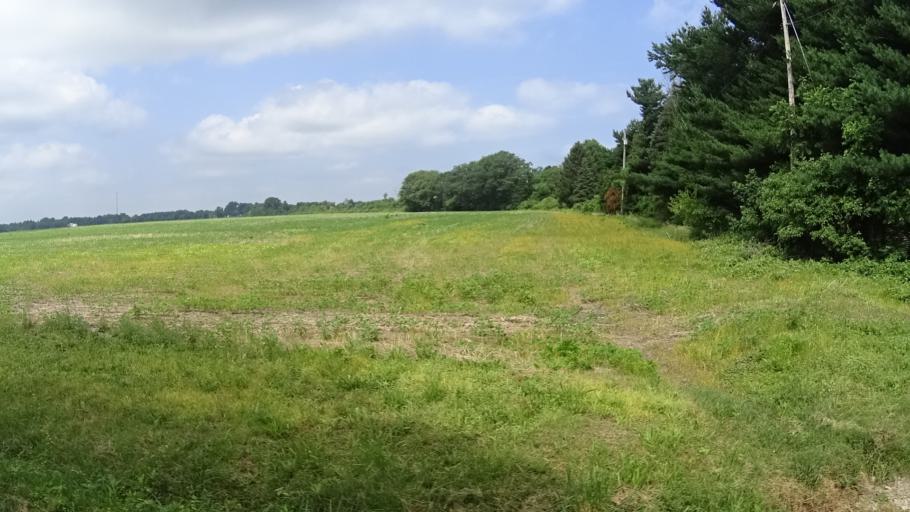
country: US
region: Ohio
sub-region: Lorain County
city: Vermilion
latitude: 41.3930
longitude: -82.4190
